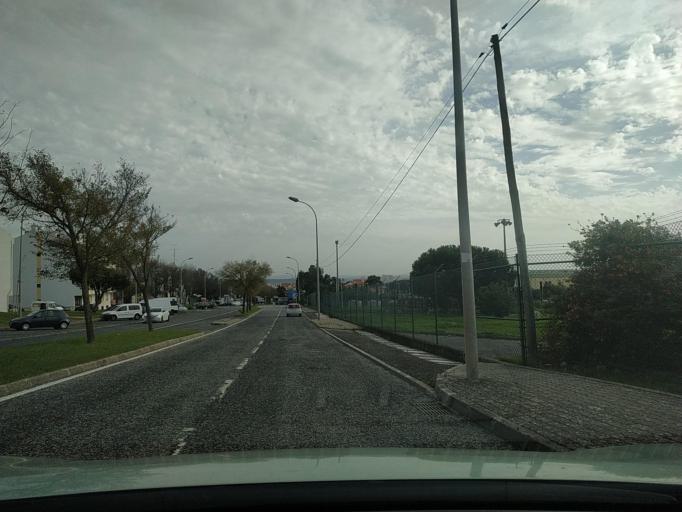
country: PT
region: Lisbon
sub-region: Sintra
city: Belas
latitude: 38.7800
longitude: -9.2367
